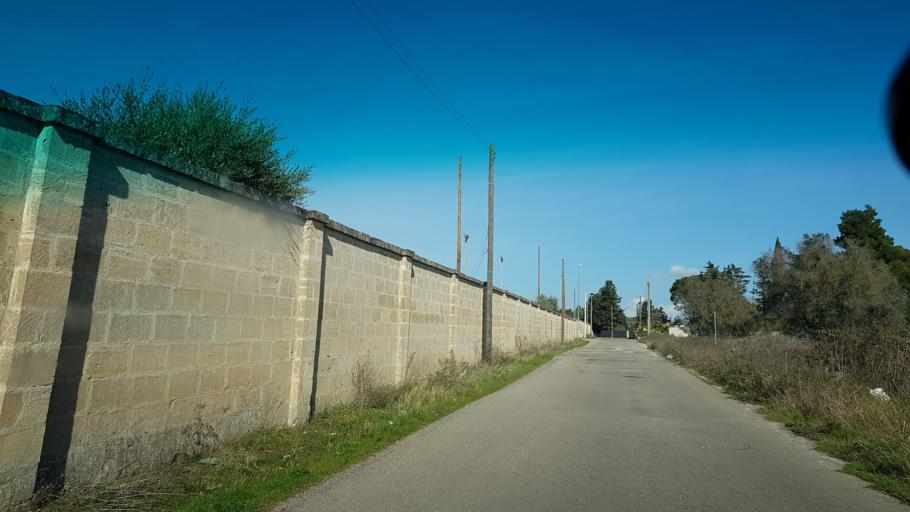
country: IT
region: Apulia
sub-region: Provincia di Lecce
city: Arnesano
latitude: 40.3551
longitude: 18.1049
